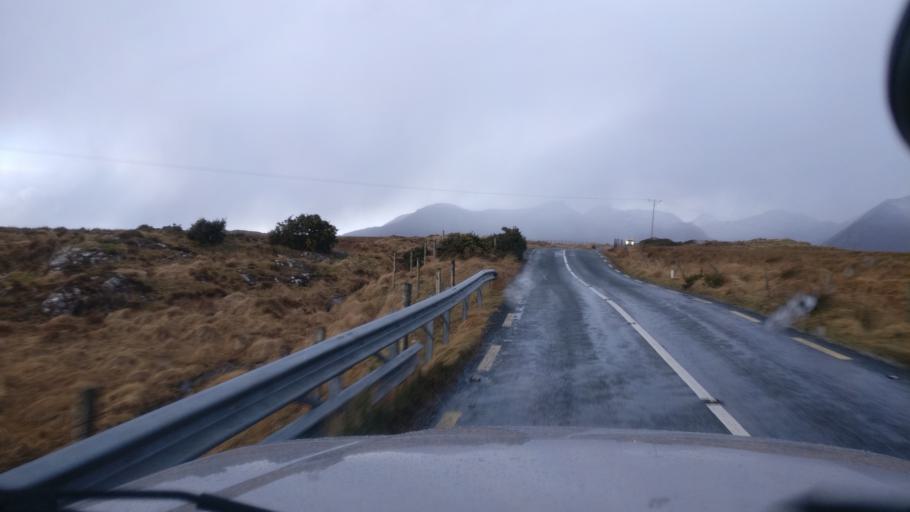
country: IE
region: Connaught
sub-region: County Galway
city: Clifden
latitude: 53.4339
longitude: -9.7682
